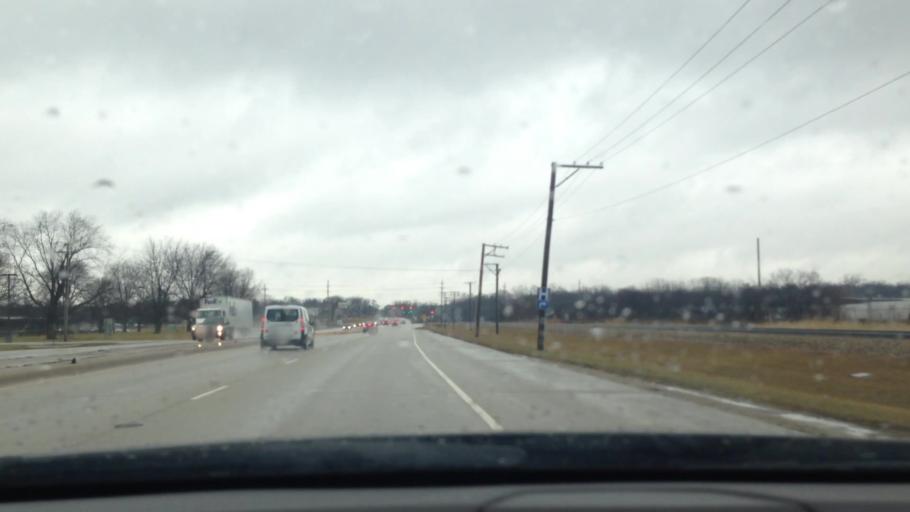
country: US
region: Illinois
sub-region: Will County
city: New Lenox
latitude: 41.5222
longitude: -88.0008
